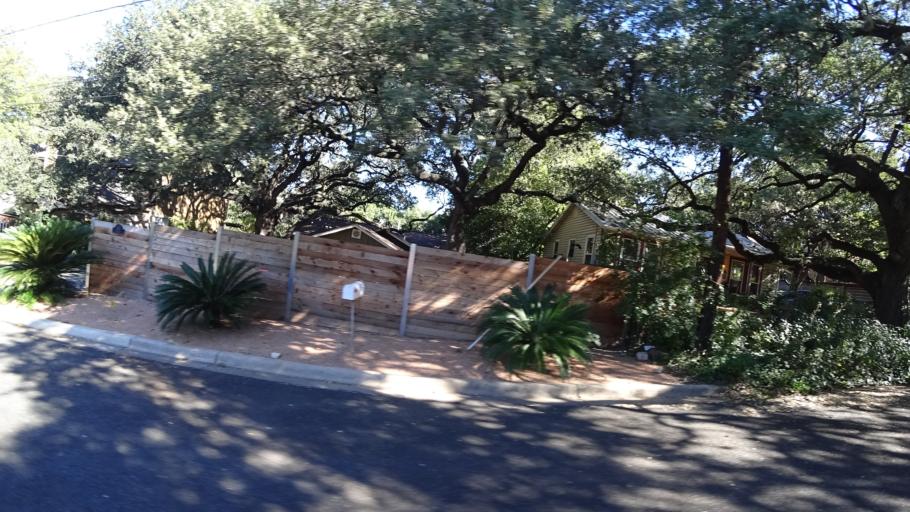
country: US
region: Texas
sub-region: Travis County
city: Austin
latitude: 30.2445
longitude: -97.7562
